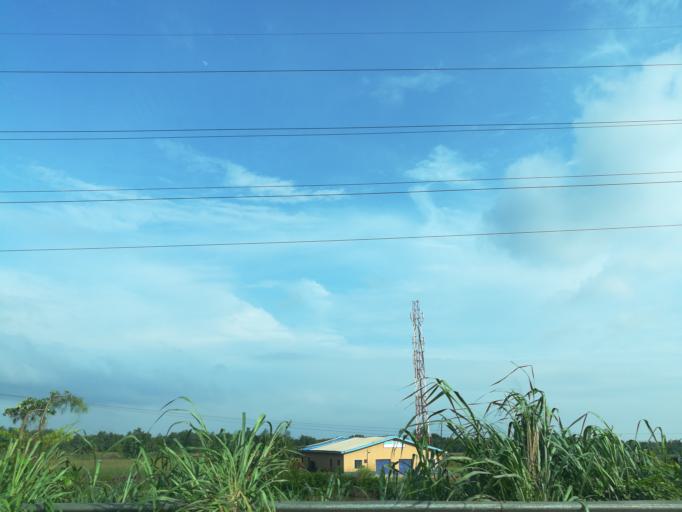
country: NG
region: Lagos
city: Ebute Ikorodu
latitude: 6.6159
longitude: 3.4464
